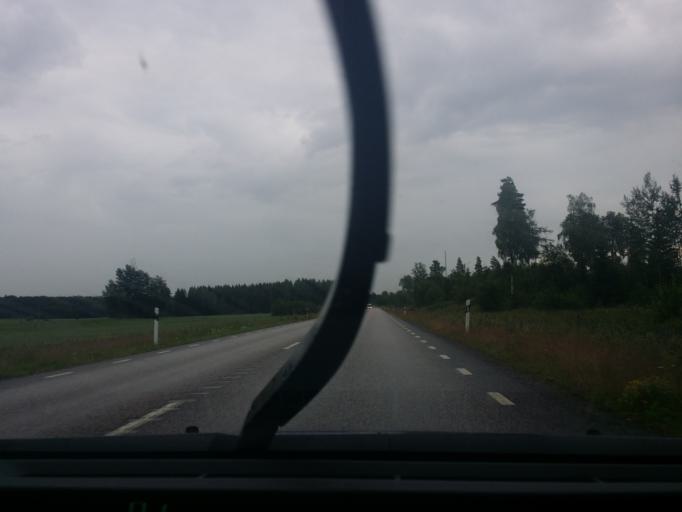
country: SE
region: OErebro
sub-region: Lindesbergs Kommun
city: Frovi
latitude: 59.4633
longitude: 15.4260
